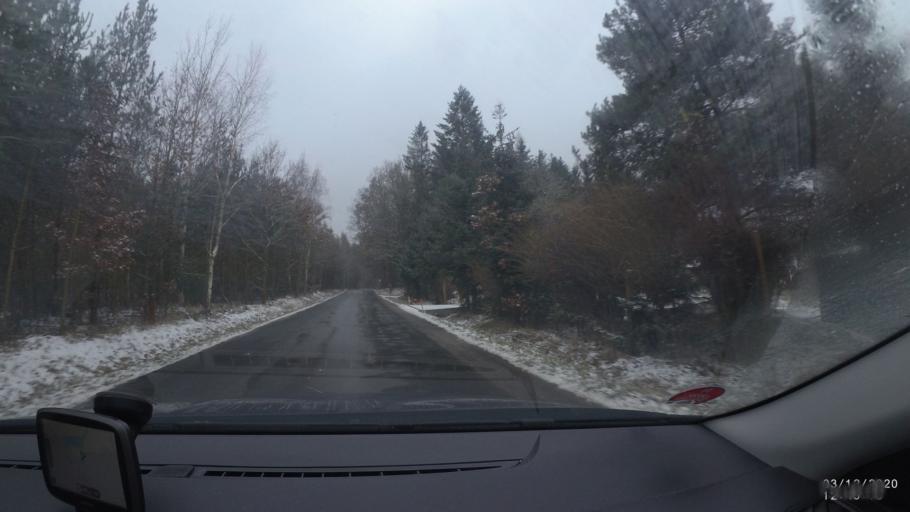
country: CZ
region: Central Bohemia
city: Revnicov
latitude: 50.1721
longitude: 13.8458
